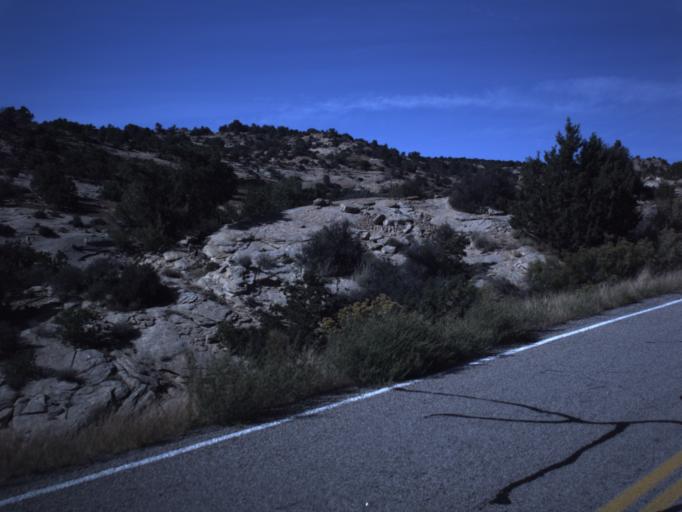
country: US
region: Utah
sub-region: San Juan County
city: Monticello
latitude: 37.9854
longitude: -109.4991
